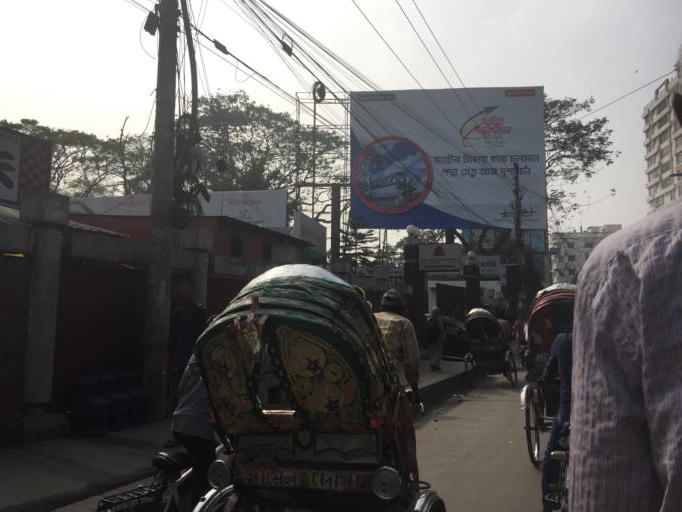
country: BD
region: Dhaka
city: Azimpur
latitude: 23.7384
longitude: 90.3769
